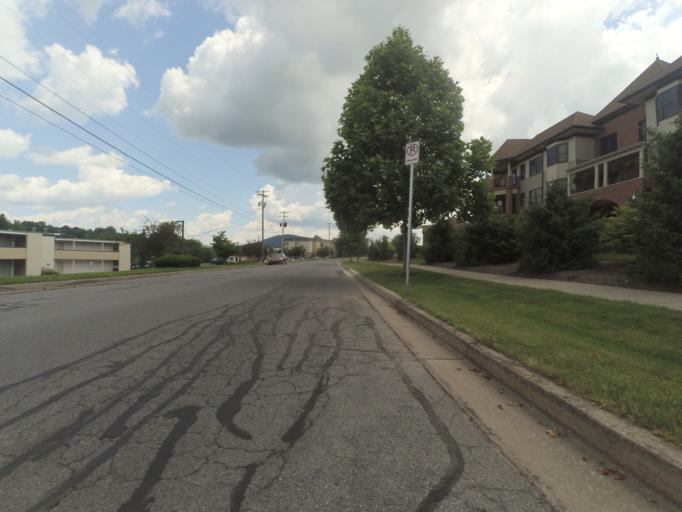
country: US
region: Pennsylvania
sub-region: Centre County
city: State College
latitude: 40.7834
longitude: -77.8392
